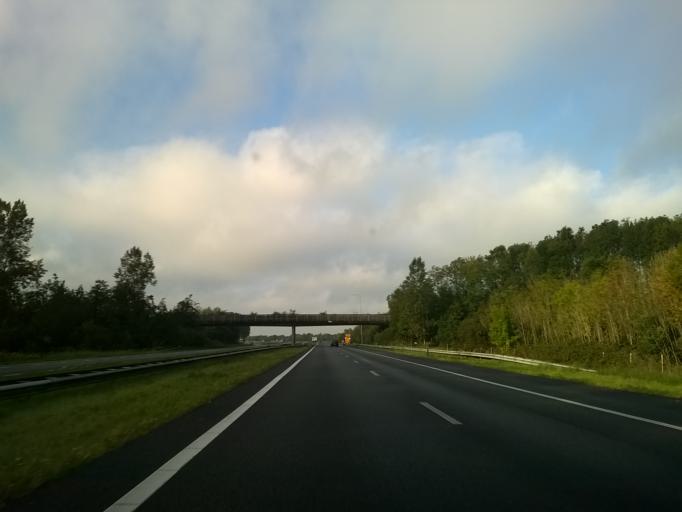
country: NL
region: Groningen
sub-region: Gemeente Grootegast
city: Grootegast
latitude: 53.1645
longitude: 6.3016
